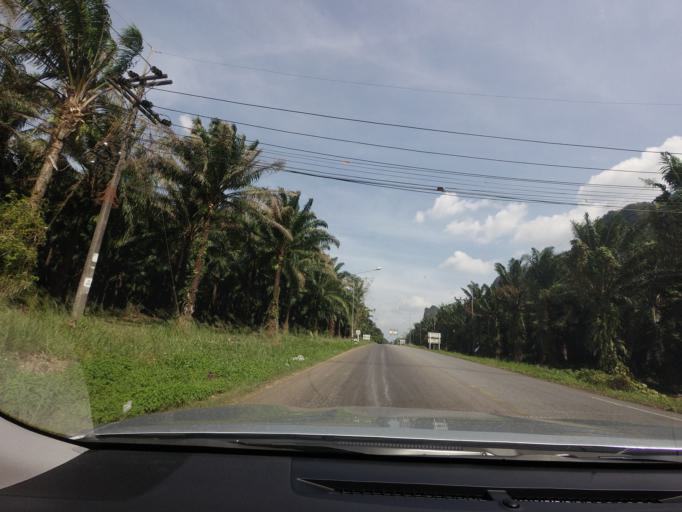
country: TH
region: Phangnga
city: Ban Ao Nang
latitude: 8.1468
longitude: 98.8119
